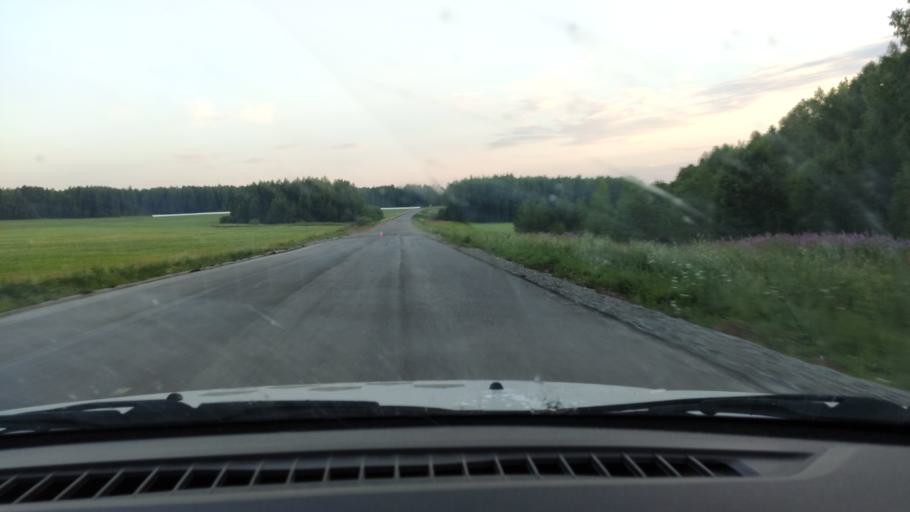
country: RU
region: Perm
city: Siva
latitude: 58.4559
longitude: 54.4127
